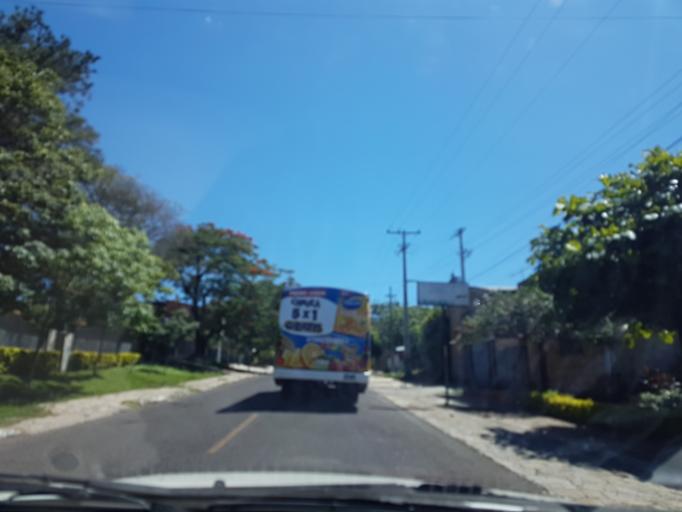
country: PY
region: Cordillera
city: Altos
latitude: -25.2602
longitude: -57.2486
